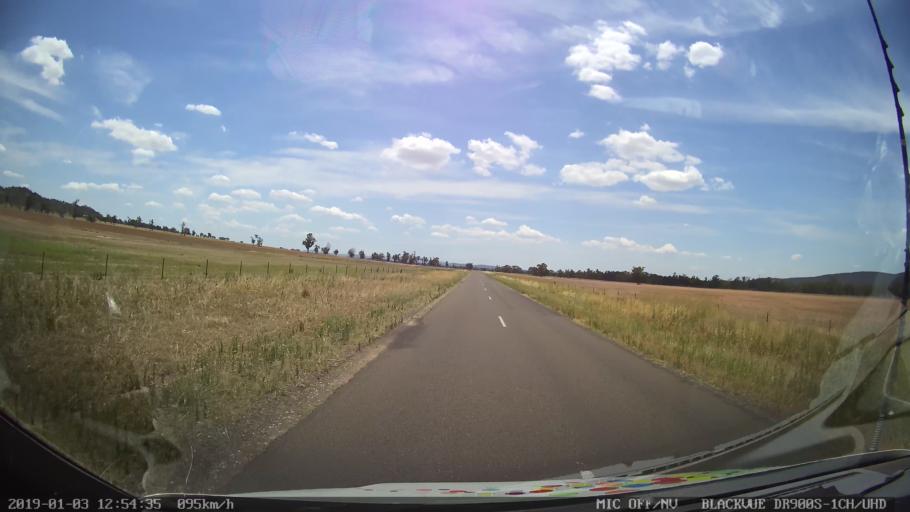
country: AU
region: New South Wales
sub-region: Weddin
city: Grenfell
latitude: -33.6513
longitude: 148.3189
